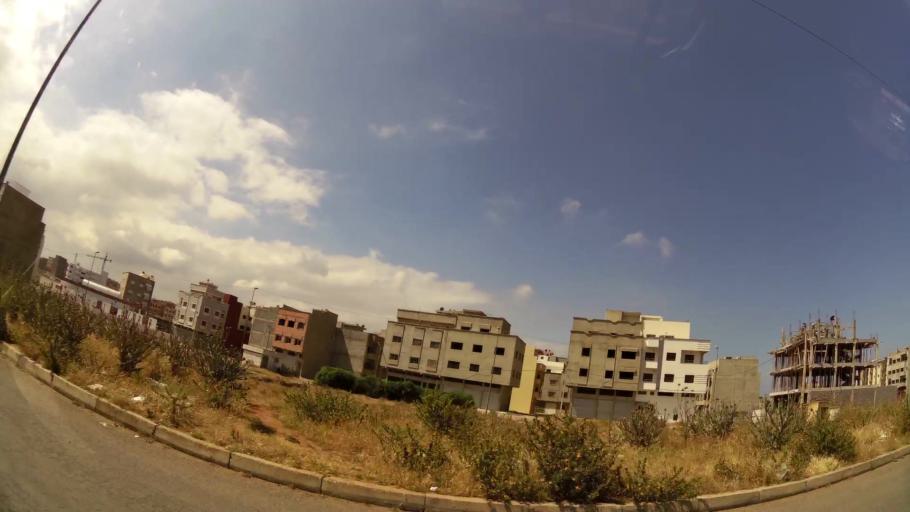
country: MA
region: Rabat-Sale-Zemmour-Zaer
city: Sale
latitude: 34.0741
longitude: -6.7708
